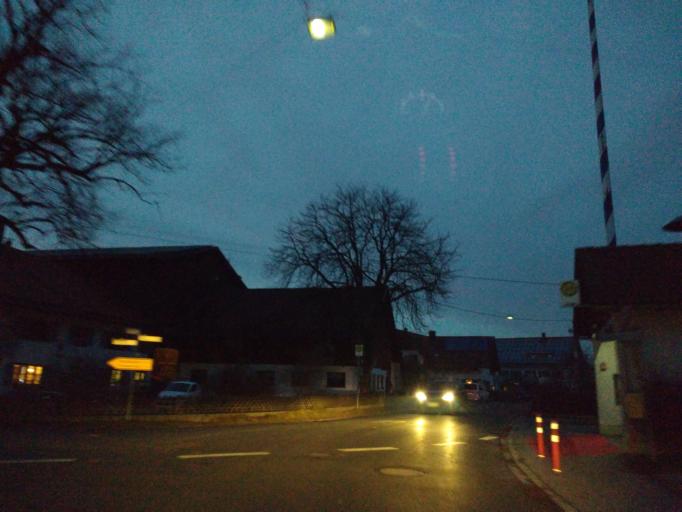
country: DE
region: Bavaria
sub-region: Swabia
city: Mauerstetten
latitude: 47.8701
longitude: 10.6904
